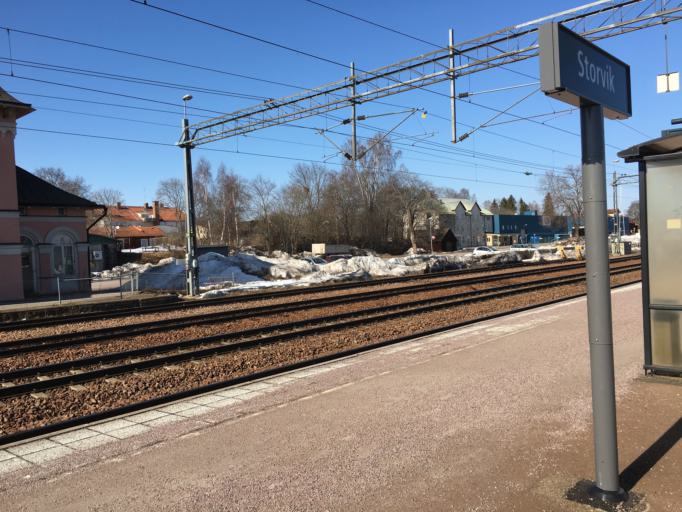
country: SE
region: Gaevleborg
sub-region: Sandvikens Kommun
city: Jarbo
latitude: 60.5821
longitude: 16.5349
